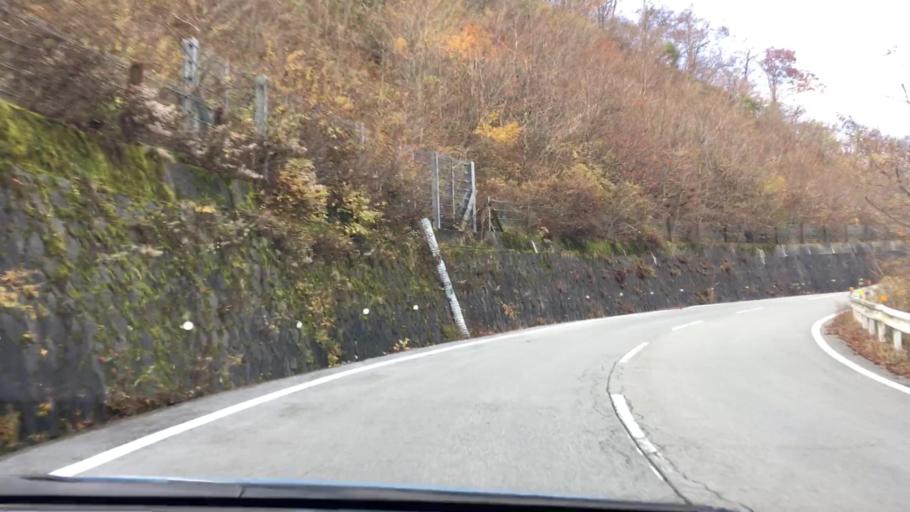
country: JP
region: Shizuoka
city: Gotemba
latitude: 35.4042
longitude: 138.9171
